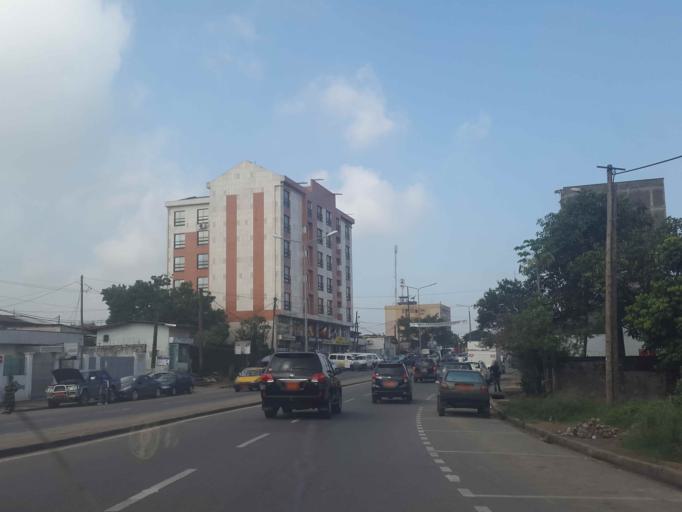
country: CM
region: Littoral
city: Douala
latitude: 4.0431
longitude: 9.6963
